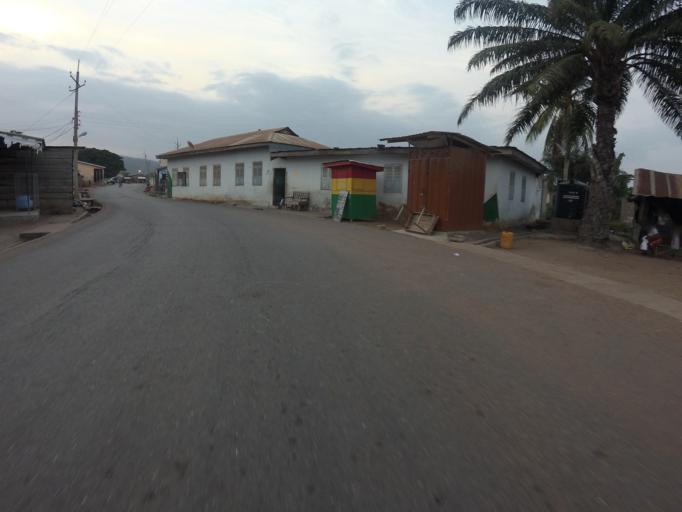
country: GH
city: Akropong
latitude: 6.1007
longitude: -0.0137
